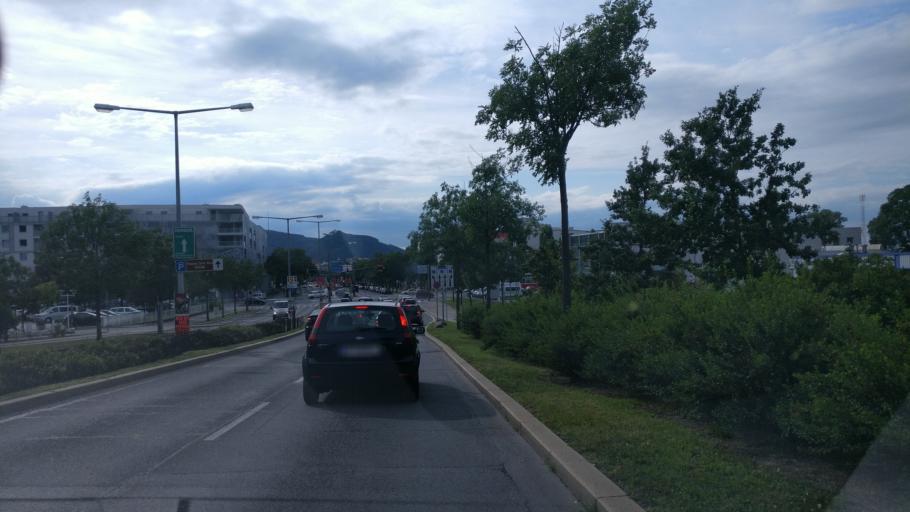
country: AT
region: Lower Austria
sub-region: Politischer Bezirk Korneuburg
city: Langenzersdorf
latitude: 48.2647
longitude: 16.4040
